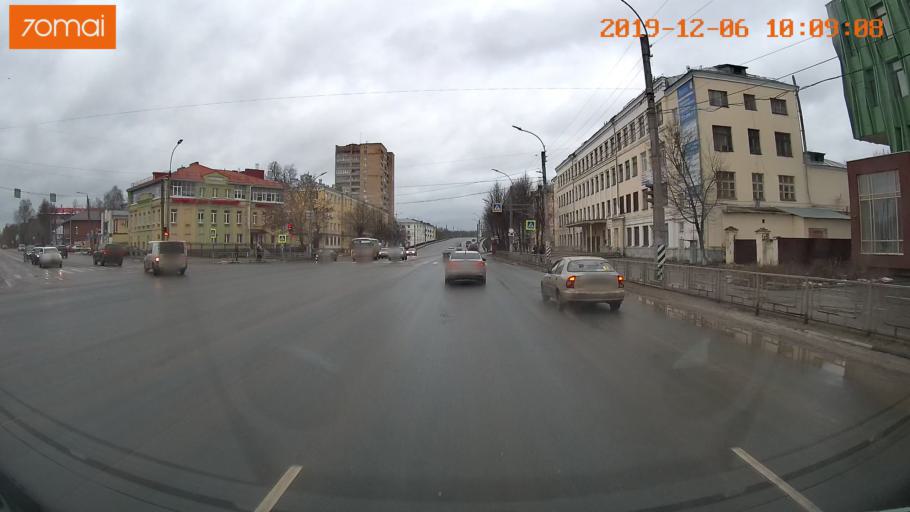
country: RU
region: Ivanovo
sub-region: Gorod Ivanovo
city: Ivanovo
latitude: 57.0209
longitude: 40.9682
